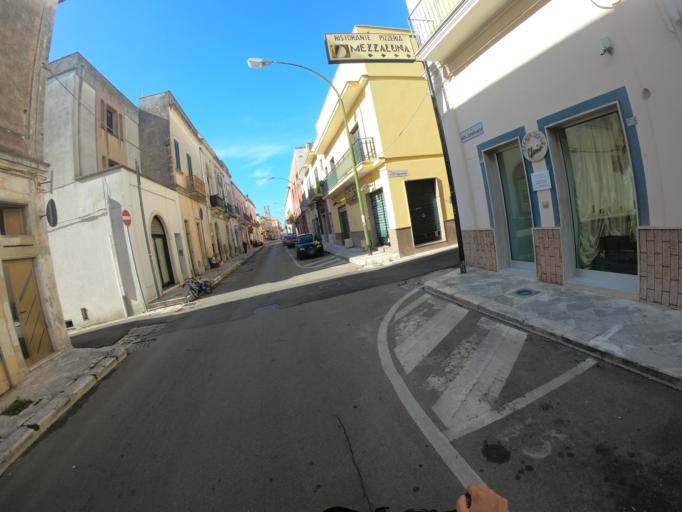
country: IT
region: Apulia
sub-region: Provincia di Lecce
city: Supersano
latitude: 40.0177
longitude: 18.2405
